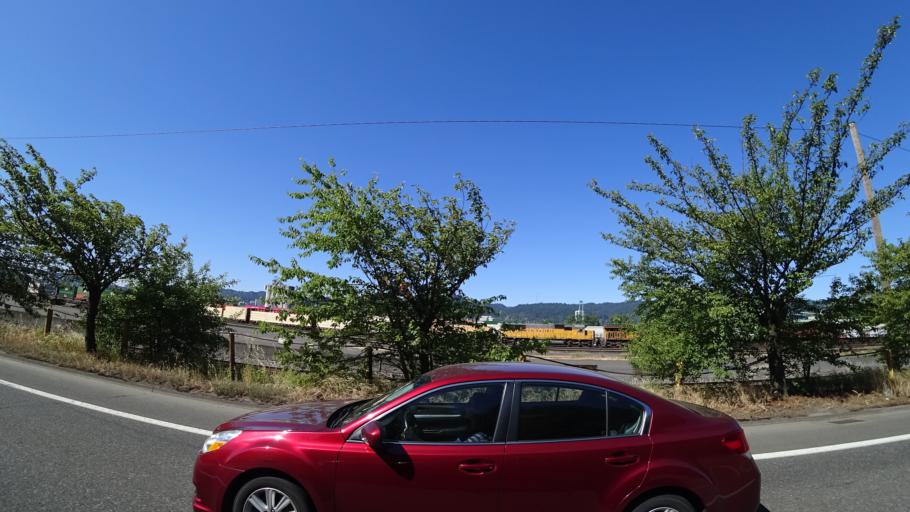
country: US
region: Oregon
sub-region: Multnomah County
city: Portland
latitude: 45.5498
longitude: -122.6873
